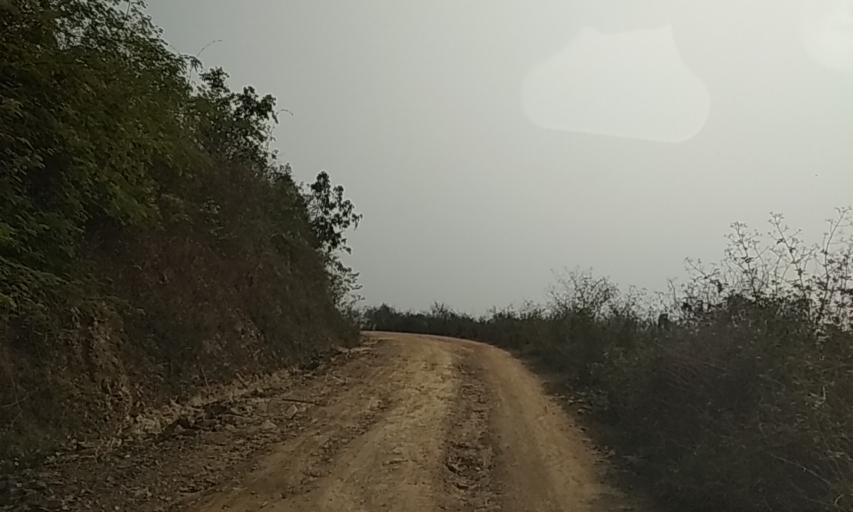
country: TH
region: Nan
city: Chaloem Phra Kiat
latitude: 19.9267
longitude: 101.1624
